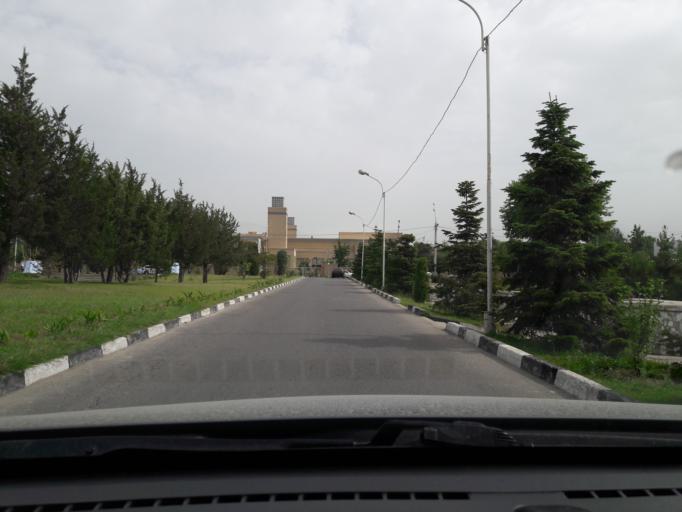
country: TJ
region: Dushanbe
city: Dushanbe
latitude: 38.5830
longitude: 68.7639
